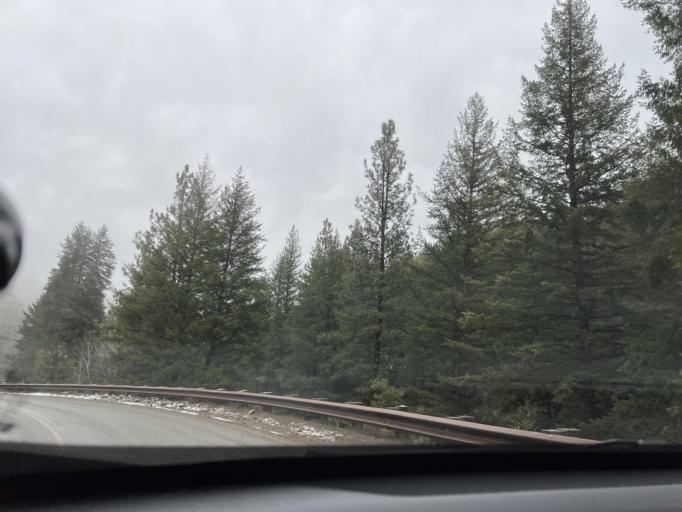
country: US
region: Washington
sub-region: Chelan County
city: Granite Falls
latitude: 48.4344
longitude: -120.2229
